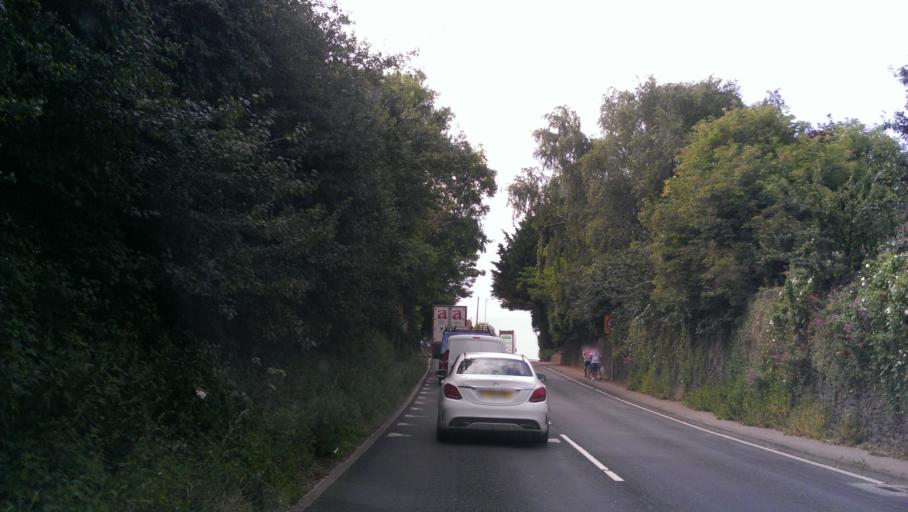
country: GB
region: England
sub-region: Kent
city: Teynham
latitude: 51.3261
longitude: 0.8066
